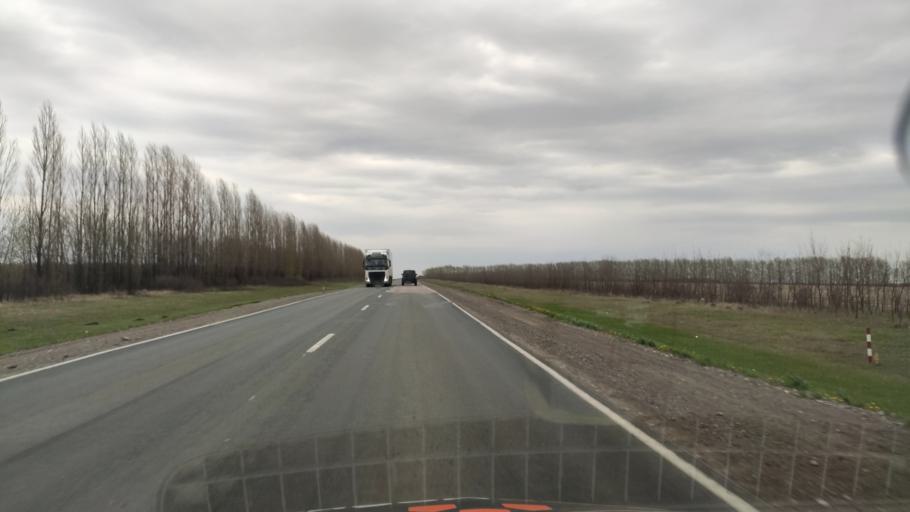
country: RU
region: Voronezj
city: Nizhnedevitsk
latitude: 51.5684
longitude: 38.2785
